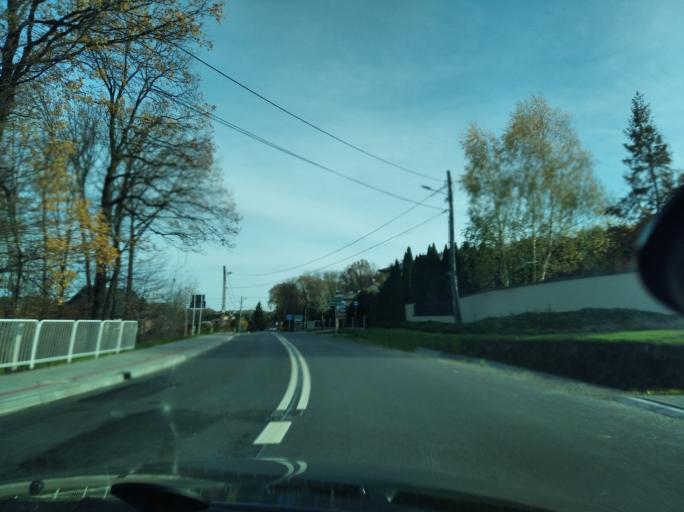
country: PL
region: Subcarpathian Voivodeship
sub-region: Powiat rzeszowski
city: Krasne
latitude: 50.0041
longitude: 22.0839
